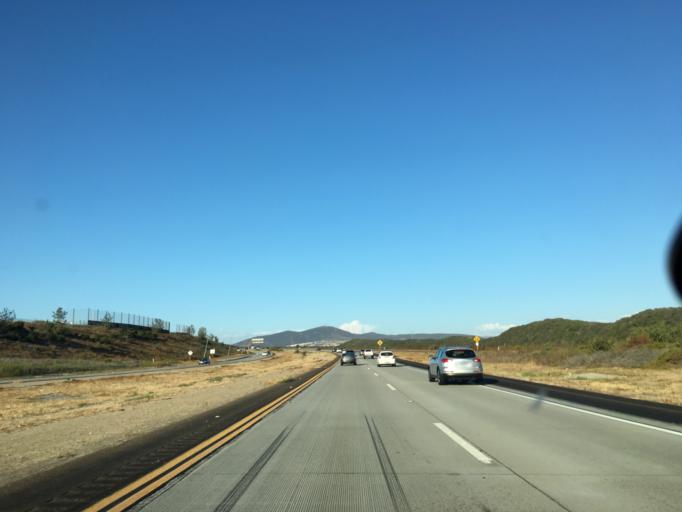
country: US
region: California
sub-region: San Diego County
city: Fairbanks Ranch
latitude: 32.9526
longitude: -117.1926
